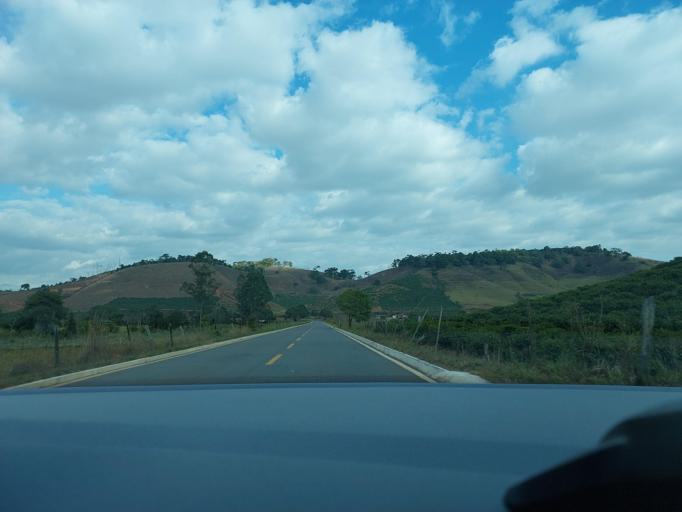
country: BR
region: Minas Gerais
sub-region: Vicosa
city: Vicosa
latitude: -20.8480
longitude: -42.6751
